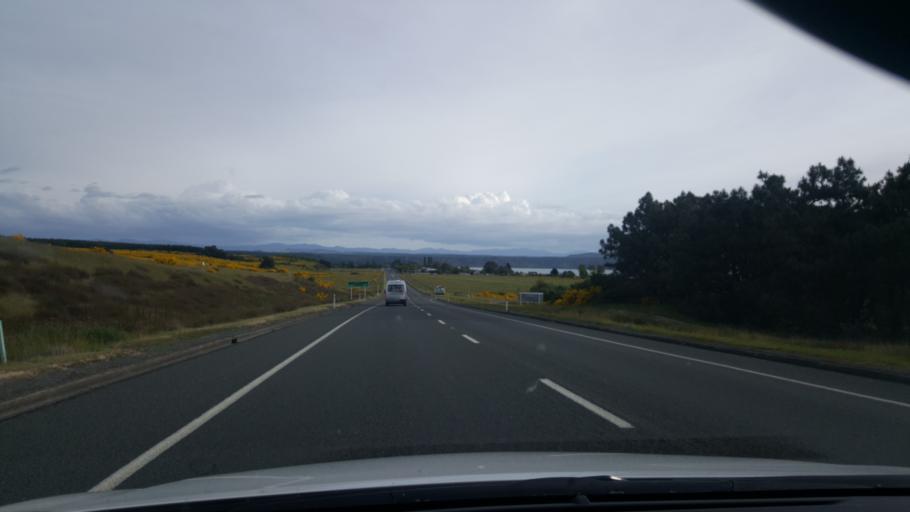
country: NZ
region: Waikato
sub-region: Taupo District
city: Taupo
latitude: -38.7440
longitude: 176.0733
